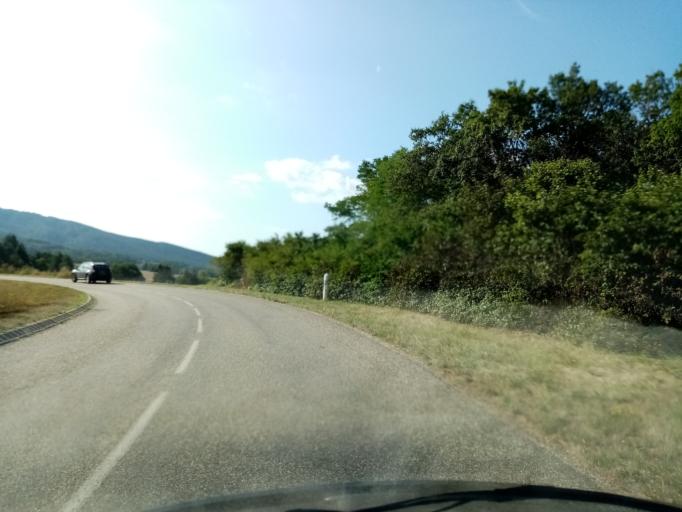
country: FR
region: Alsace
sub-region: Departement du Bas-Rhin
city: Ville
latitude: 48.3351
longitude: 7.3448
